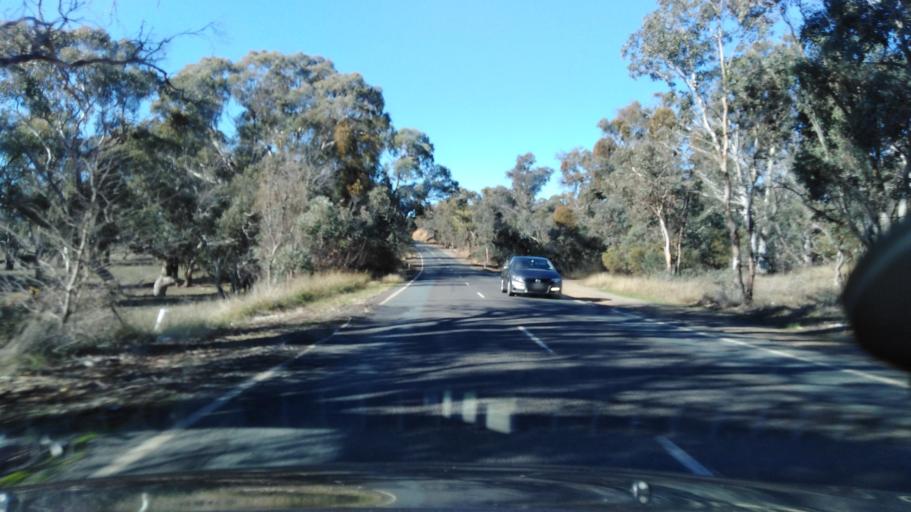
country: AU
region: New South Wales
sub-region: Yass Valley
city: Gundaroo
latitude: -35.1816
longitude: 149.2838
